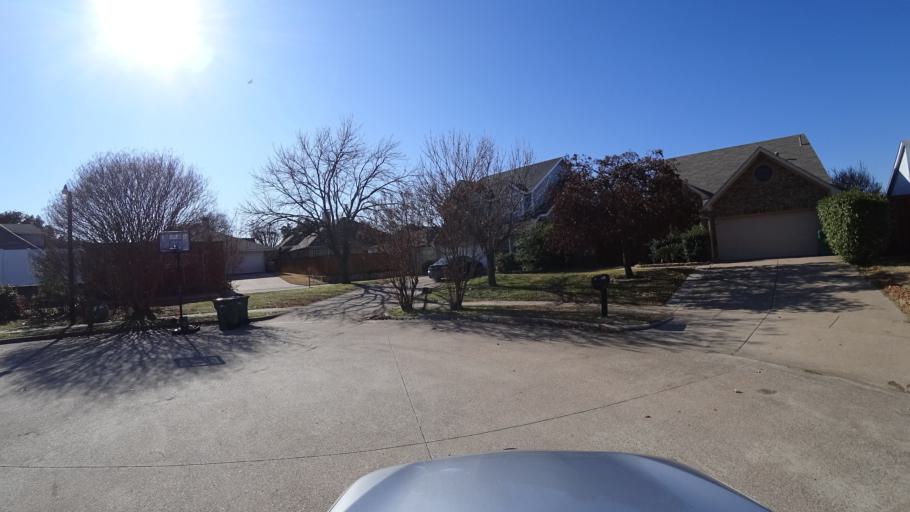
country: US
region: Texas
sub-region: Denton County
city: Lewisville
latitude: 33.0113
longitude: -97.0209
